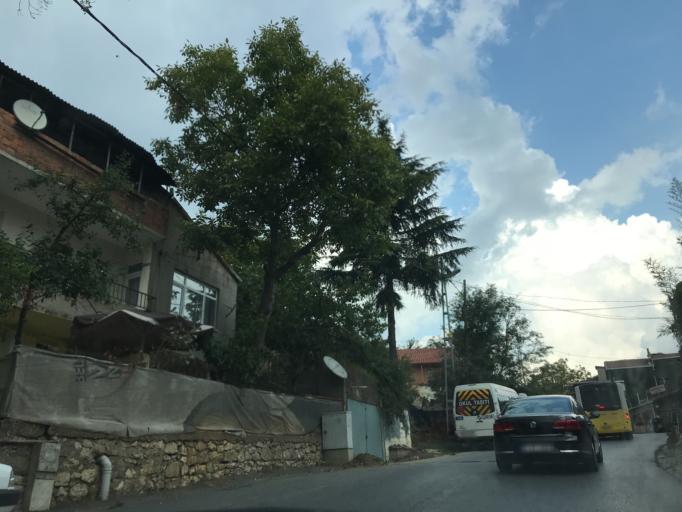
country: TR
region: Istanbul
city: Arikoey
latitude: 41.1766
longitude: 29.0511
